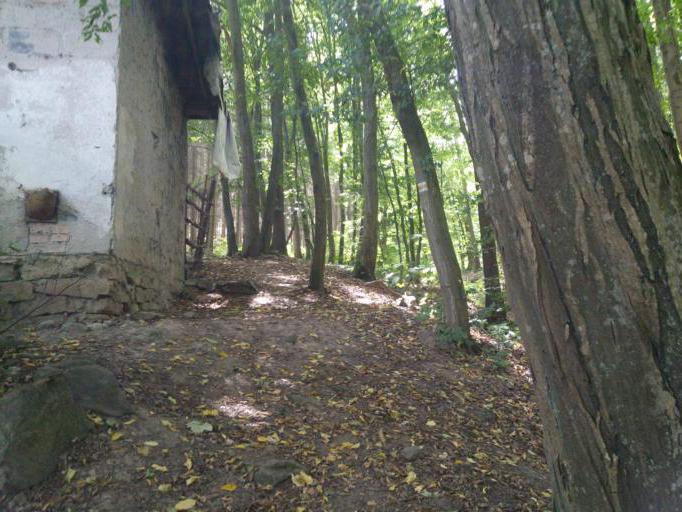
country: CZ
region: South Moravian
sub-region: Okres Znojmo
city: Jevisovice
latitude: 49.0330
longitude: 15.9828
